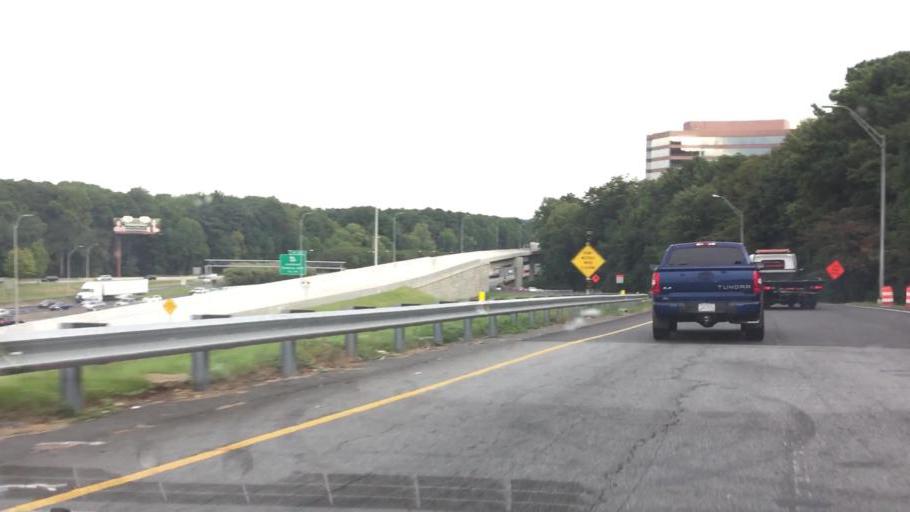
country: US
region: Georgia
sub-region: Cobb County
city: Fair Oaks
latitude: 33.9398
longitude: -84.5049
